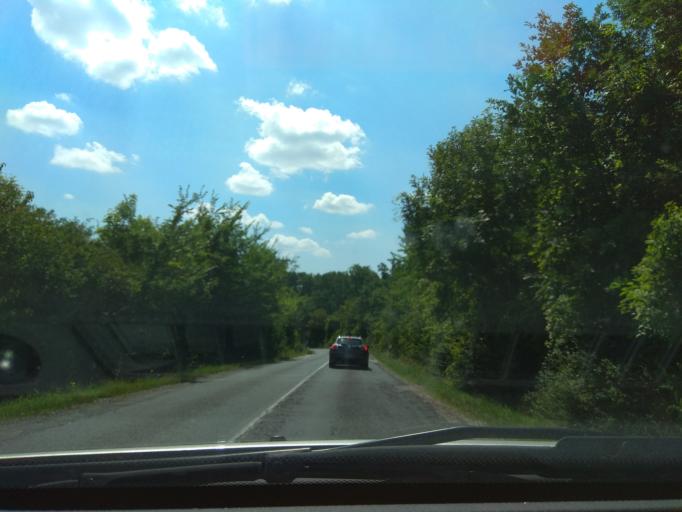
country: HU
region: Borsod-Abauj-Zemplen
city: Harsany
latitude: 48.0159
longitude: 20.7641
